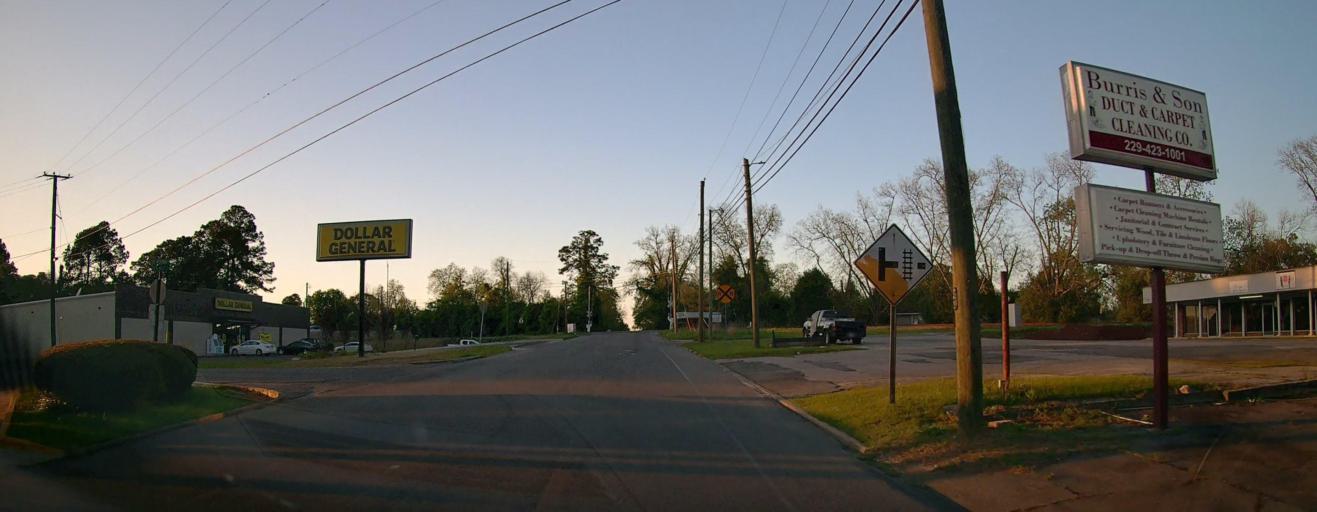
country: US
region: Georgia
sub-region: Ben Hill County
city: Fitzgerald
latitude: 31.7178
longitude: -83.2649
